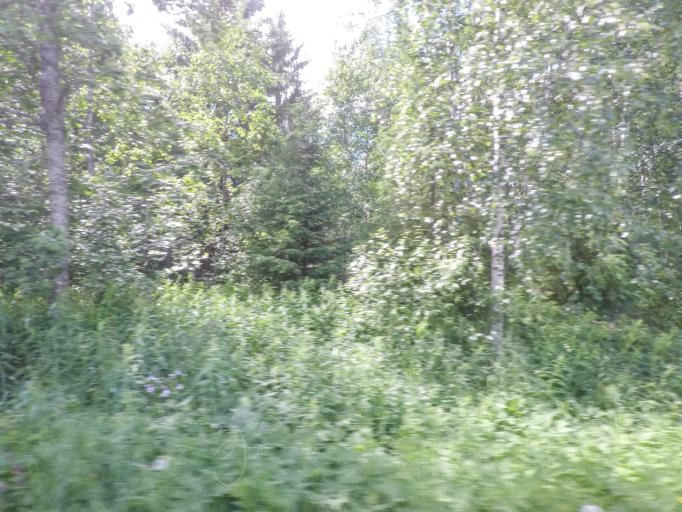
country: FI
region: Central Finland
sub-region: Jyvaeskylae
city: Hankasalmi
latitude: 62.4143
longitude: 26.6427
